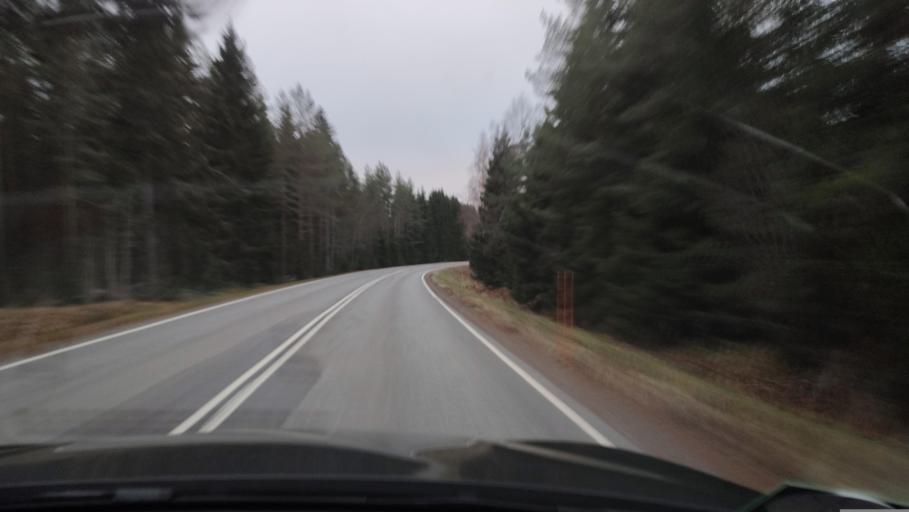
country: FI
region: Southern Ostrobothnia
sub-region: Suupohja
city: Karijoki
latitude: 62.3233
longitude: 21.7577
